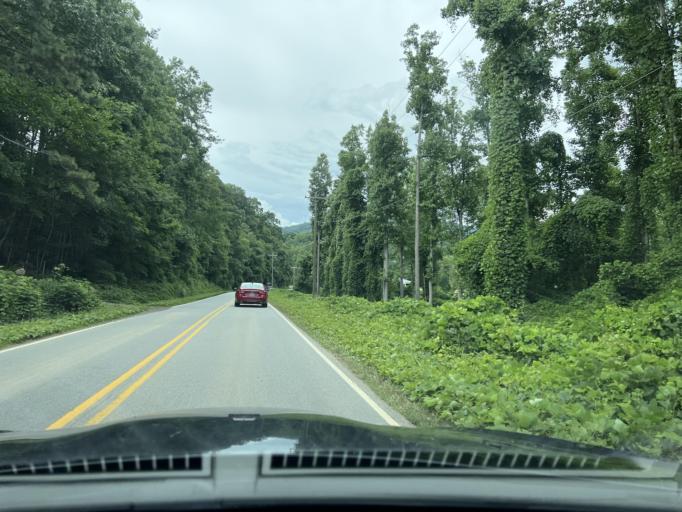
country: US
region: North Carolina
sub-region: Henderson County
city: Fruitland
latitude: 35.4100
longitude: -82.4098
